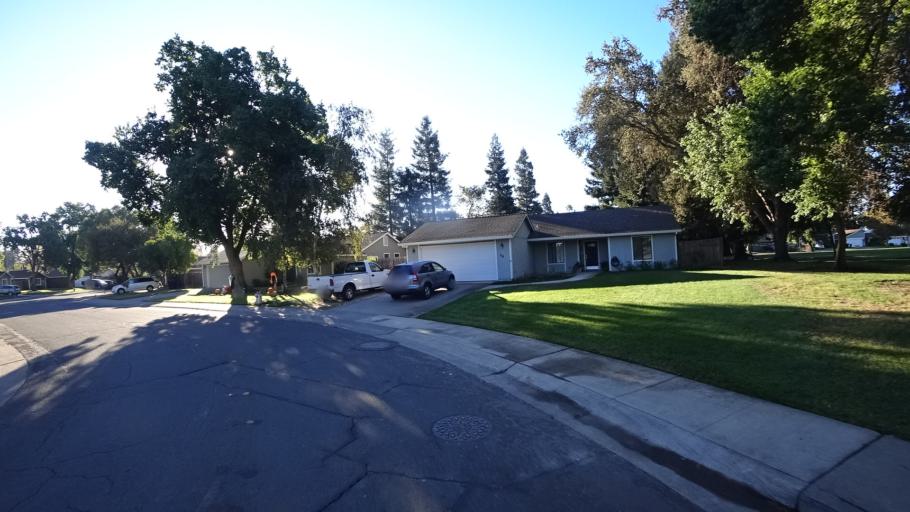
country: US
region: California
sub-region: Sacramento County
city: Parkway
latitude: 38.4876
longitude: -121.5418
